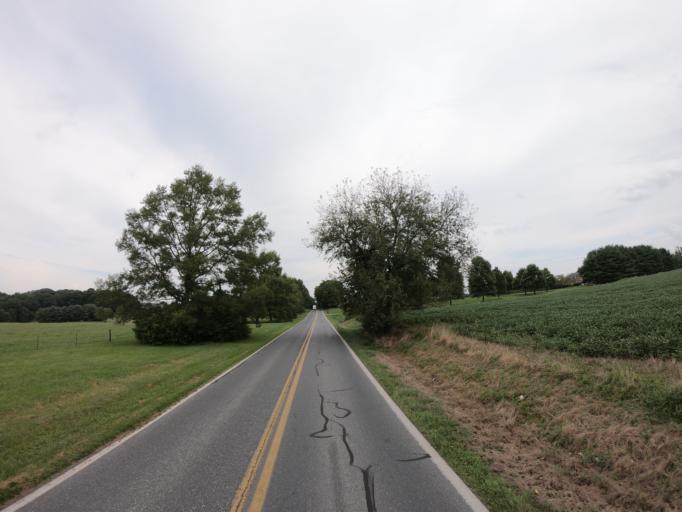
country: US
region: Maryland
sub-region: Montgomery County
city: Redland
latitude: 39.2153
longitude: -77.1178
